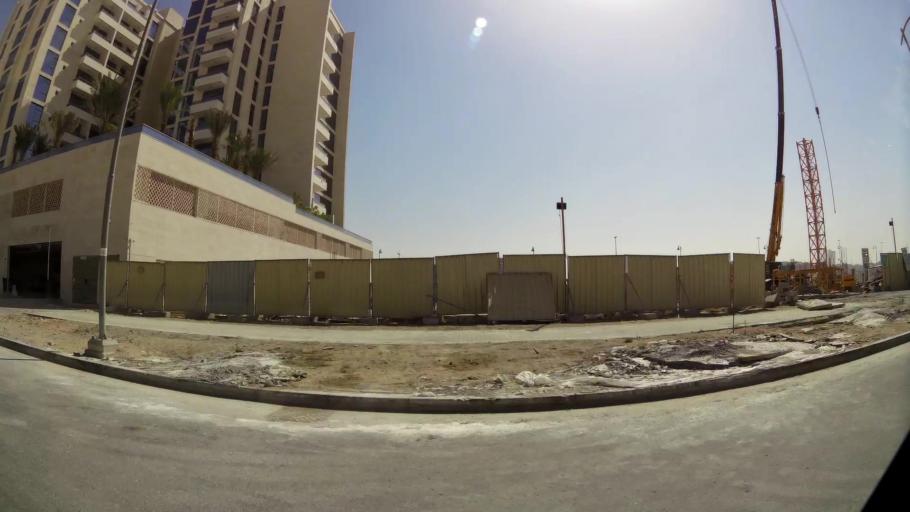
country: AE
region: Dubai
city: Dubai
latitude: 25.0374
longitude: 55.1406
